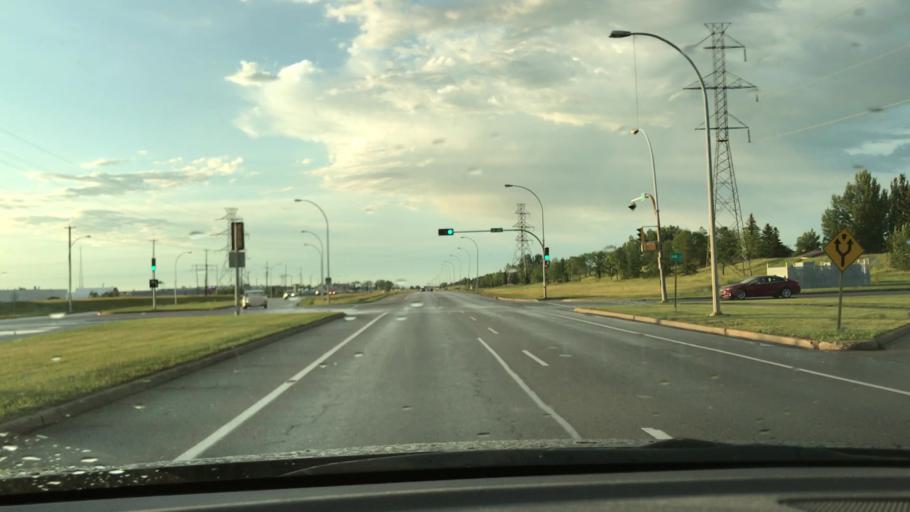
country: CA
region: Alberta
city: Edmonton
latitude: 53.4583
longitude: -113.4664
